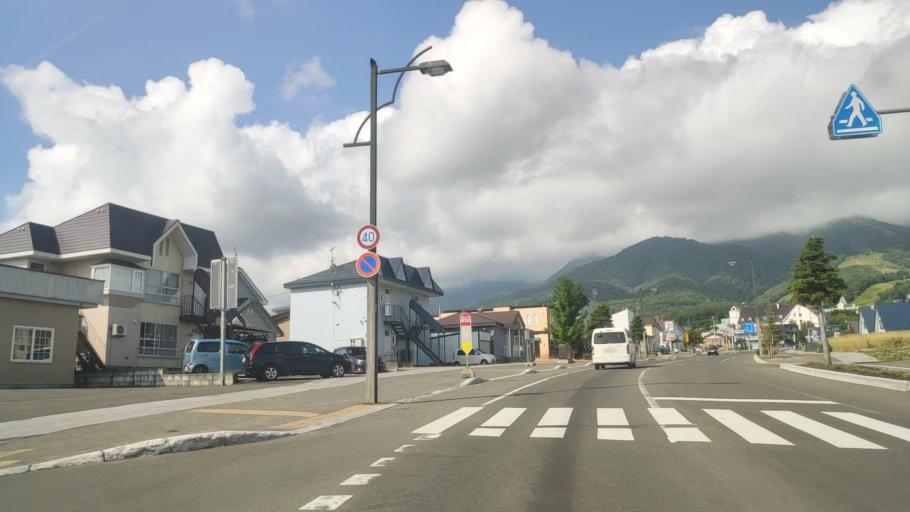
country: JP
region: Hokkaido
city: Shimo-furano
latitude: 43.3441
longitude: 142.3702
